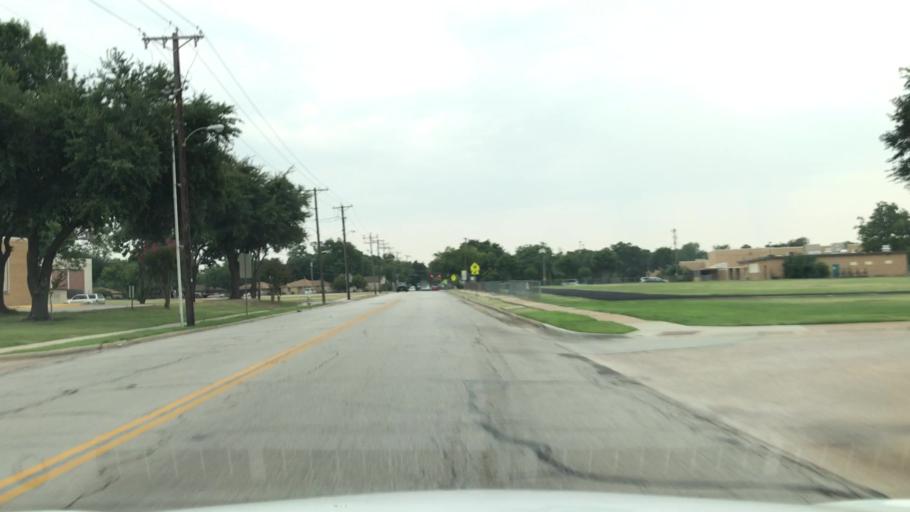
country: US
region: Texas
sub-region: Dallas County
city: Carrollton
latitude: 32.9569
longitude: -96.8954
